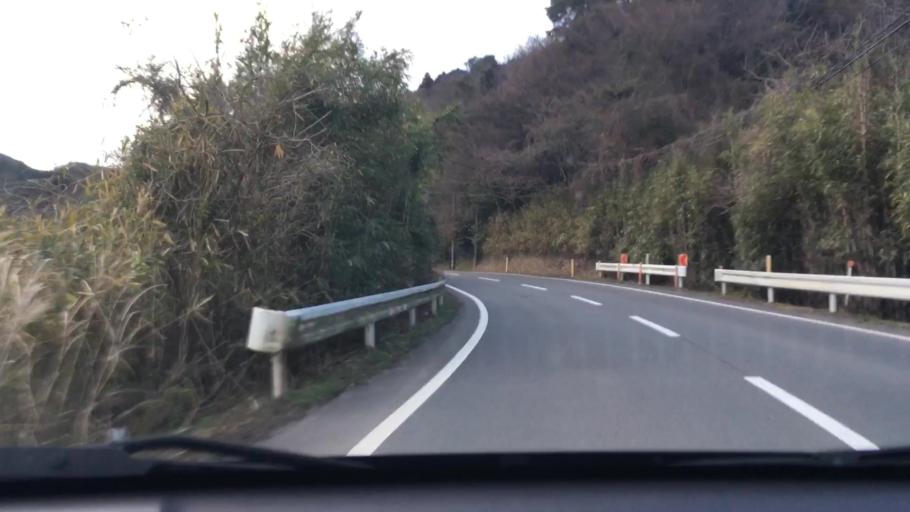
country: JP
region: Oita
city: Hiji
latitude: 33.3699
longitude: 131.4656
